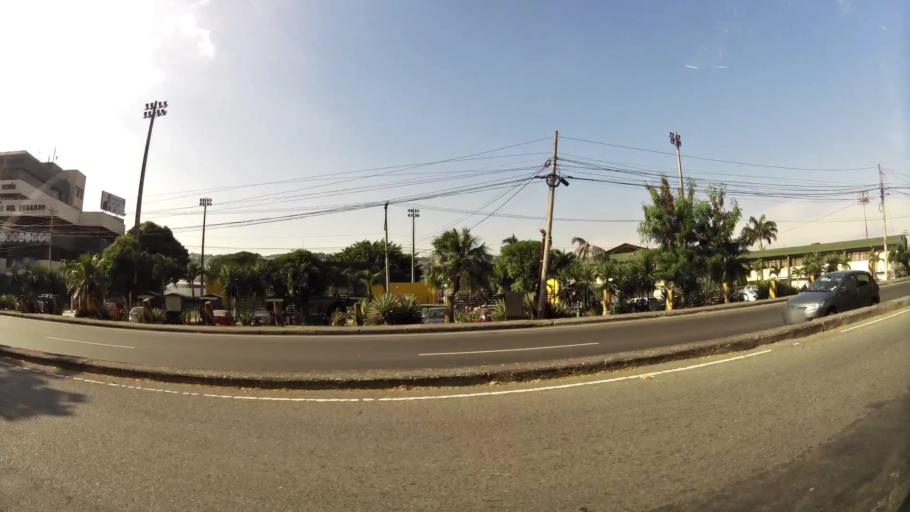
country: EC
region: Guayas
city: Guayaquil
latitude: -2.1625
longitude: -79.9249
